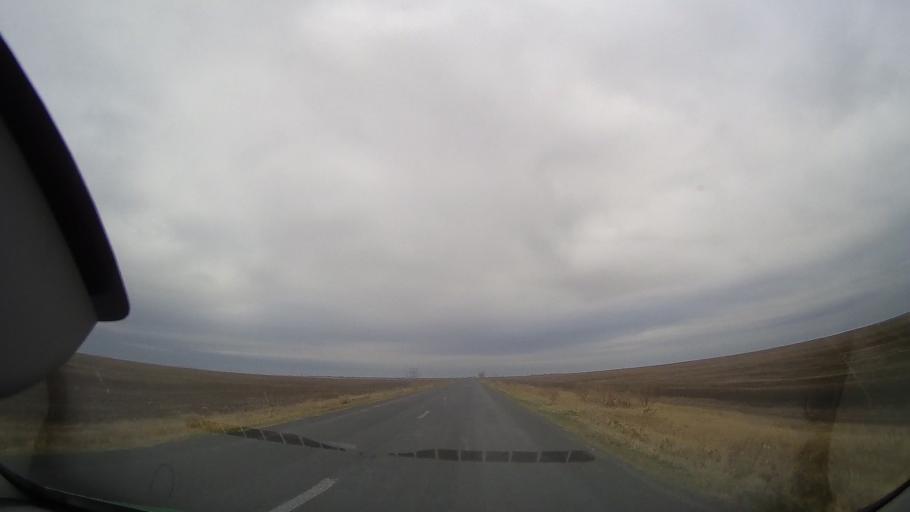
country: RO
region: Buzau
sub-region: Comuna Padina
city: Padina
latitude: 44.8119
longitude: 27.1259
